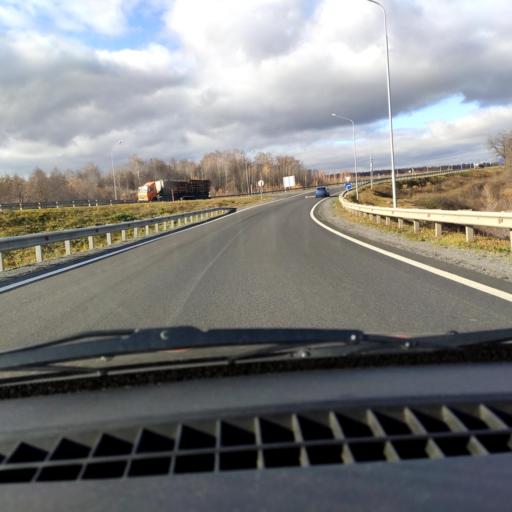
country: RU
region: Bashkortostan
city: Avdon
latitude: 54.6669
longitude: 55.7344
